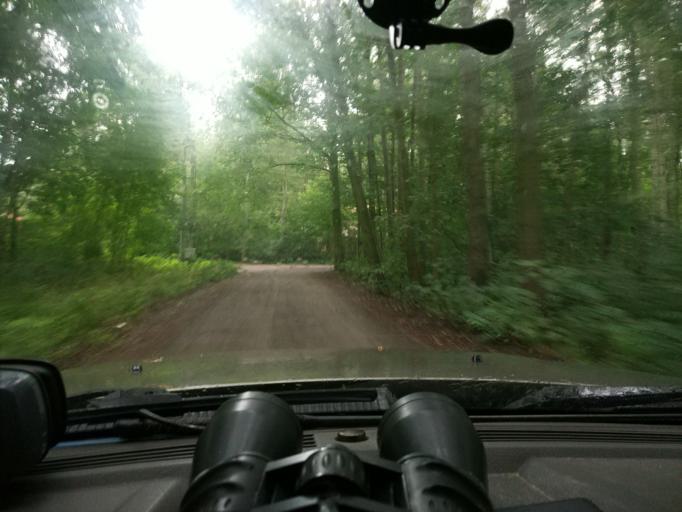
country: PL
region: Masovian Voivodeship
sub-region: Powiat grodziski
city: Podkowa Lesna
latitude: 52.1274
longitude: 20.7363
